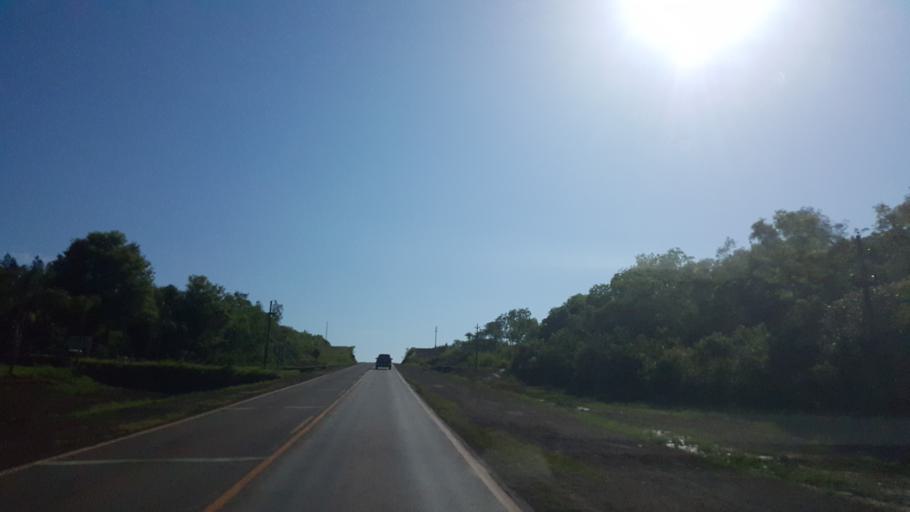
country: AR
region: Misiones
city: Santa Ana
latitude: -27.3725
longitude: -55.5685
